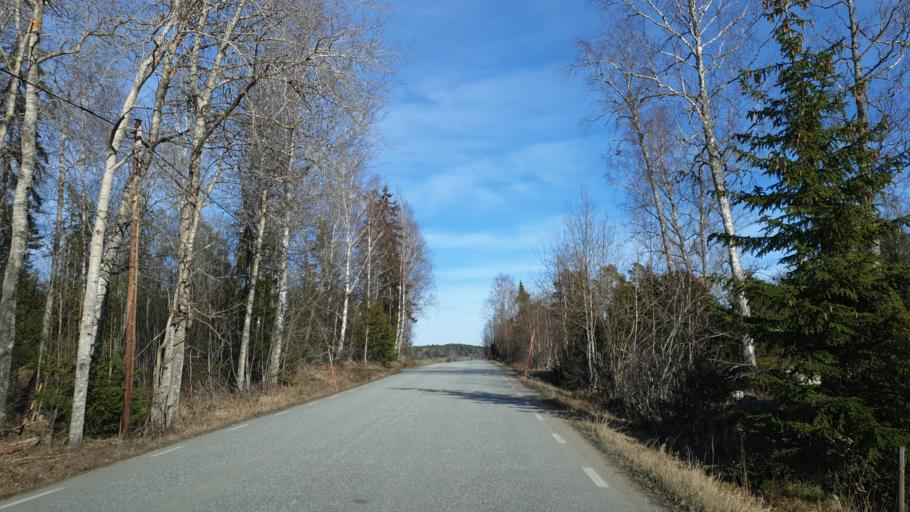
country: SE
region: Uppsala
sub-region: Enkopings Kommun
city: Grillby
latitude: 59.5505
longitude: 17.2228
